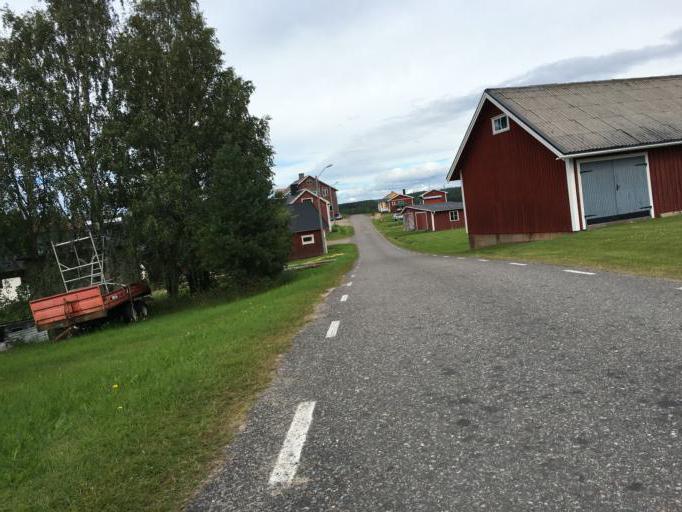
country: SE
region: Norrbotten
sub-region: Overkalix Kommun
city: OEverkalix
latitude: 66.1070
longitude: 22.7838
